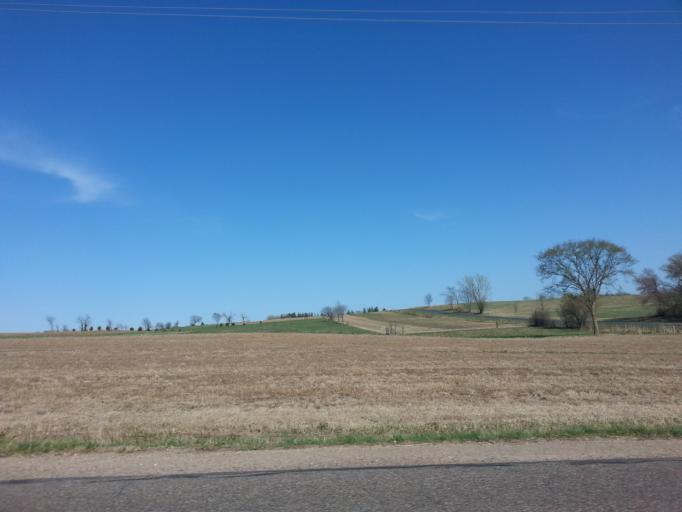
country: US
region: Wisconsin
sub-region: Pierce County
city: River Falls
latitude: 44.7910
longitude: -92.5785
